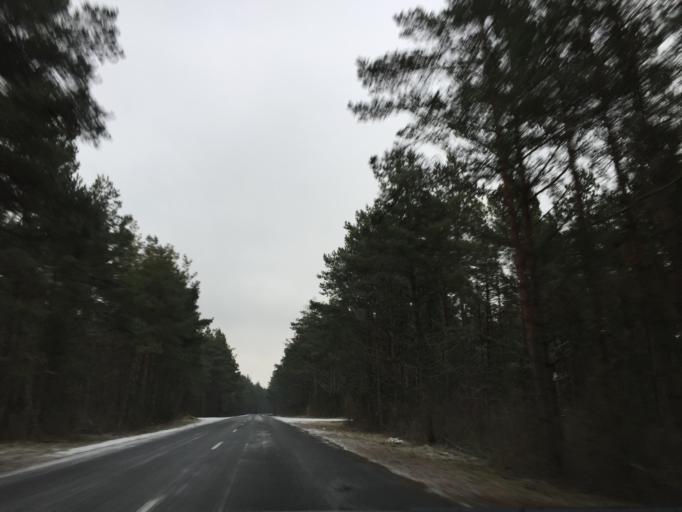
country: EE
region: Saare
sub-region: Orissaare vald
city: Orissaare
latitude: 58.5989
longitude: 23.1370
